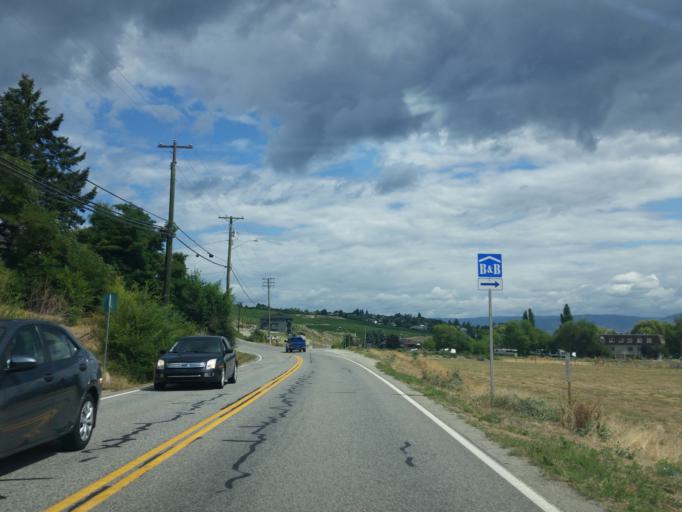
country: CA
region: British Columbia
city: West Kelowna
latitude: 49.8342
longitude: -119.5805
